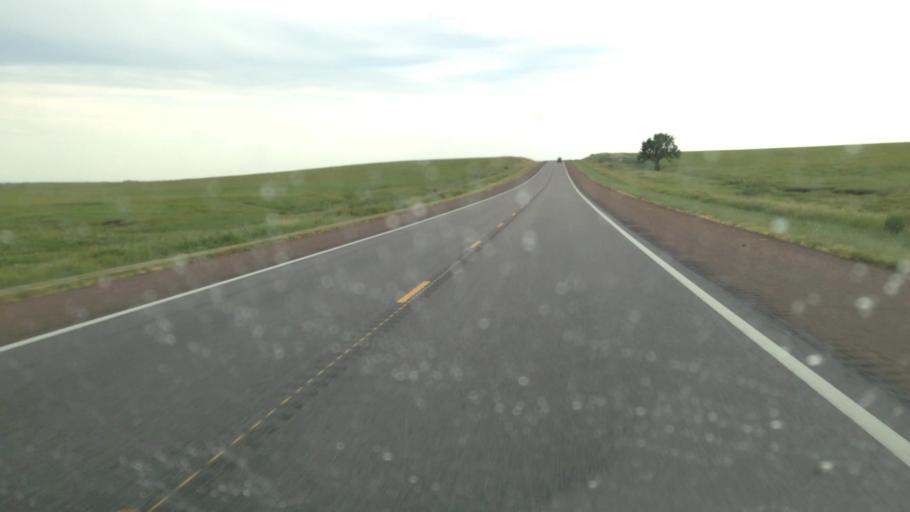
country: US
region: Kansas
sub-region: Coffey County
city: Burlington
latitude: 38.0534
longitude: -95.7391
